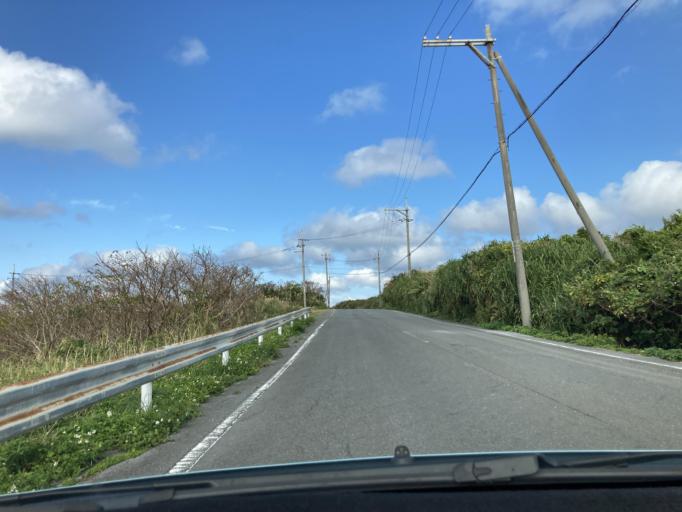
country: JP
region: Okinawa
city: Nago
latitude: 26.8674
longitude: 128.2604
